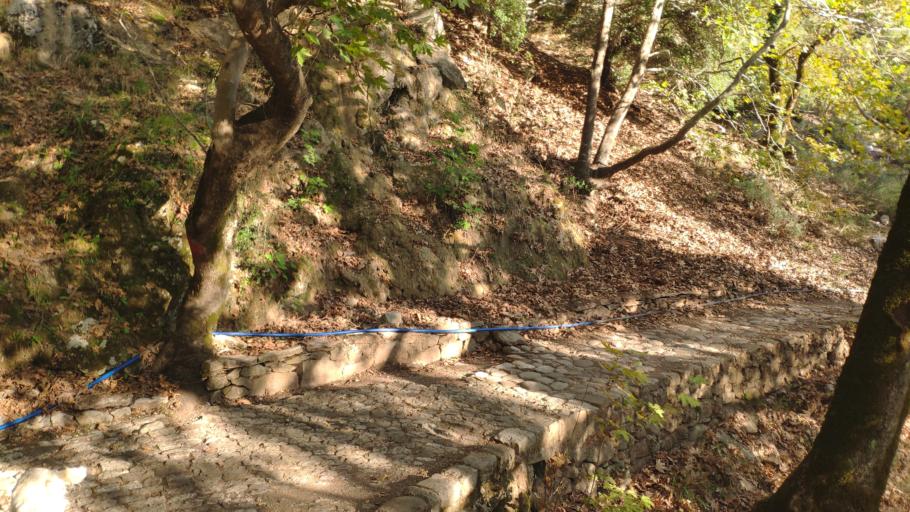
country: GR
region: Thessaly
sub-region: Trikala
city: Pyli
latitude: 39.4607
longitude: 21.6003
